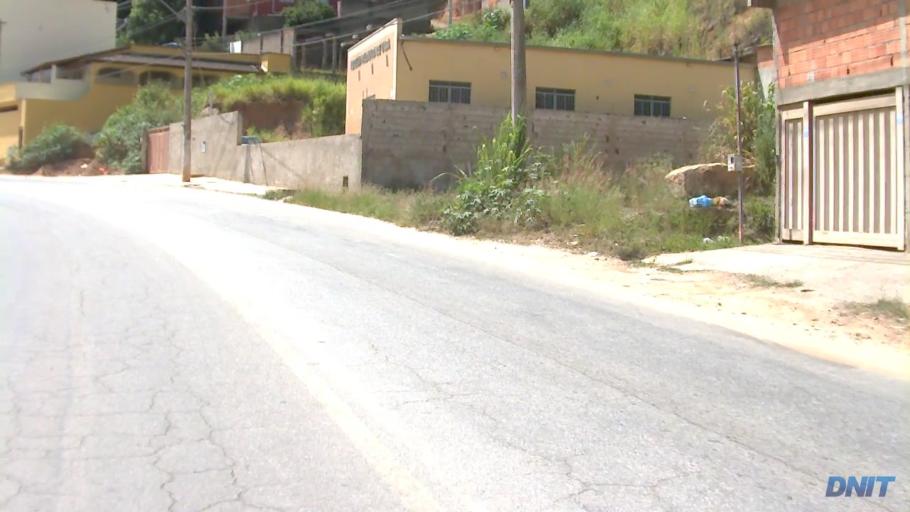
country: BR
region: Minas Gerais
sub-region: Coronel Fabriciano
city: Coronel Fabriciano
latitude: -19.5356
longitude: -42.6682
